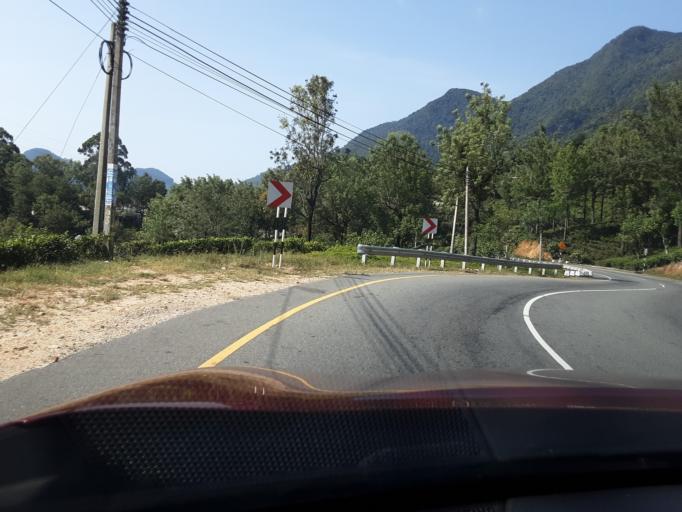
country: LK
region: Uva
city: Badulla
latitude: 6.9540
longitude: 81.1225
